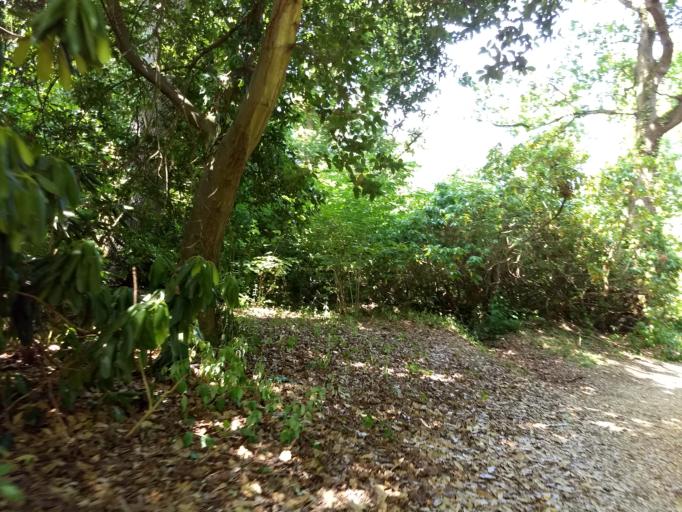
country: GB
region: England
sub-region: Isle of Wight
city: East Cowes
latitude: 50.7512
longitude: -1.2556
